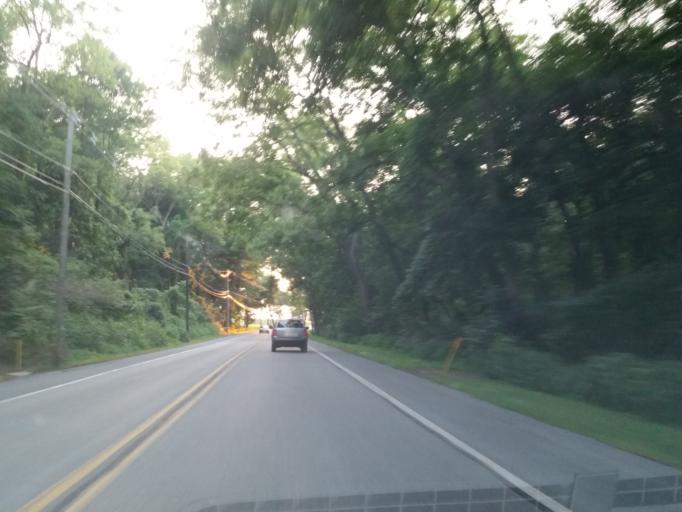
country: US
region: Pennsylvania
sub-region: Lebanon County
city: Cornwall
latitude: 40.2747
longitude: -76.4208
